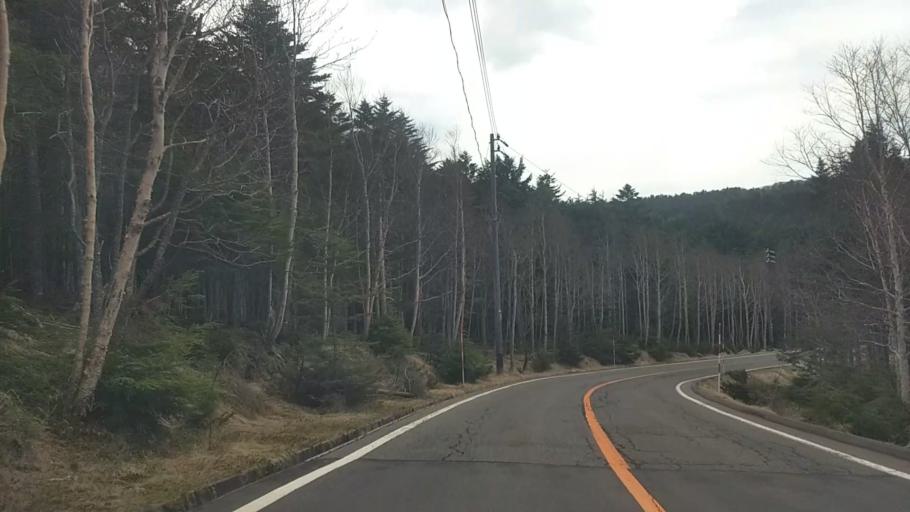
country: JP
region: Nagano
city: Saku
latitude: 36.0585
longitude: 138.3601
